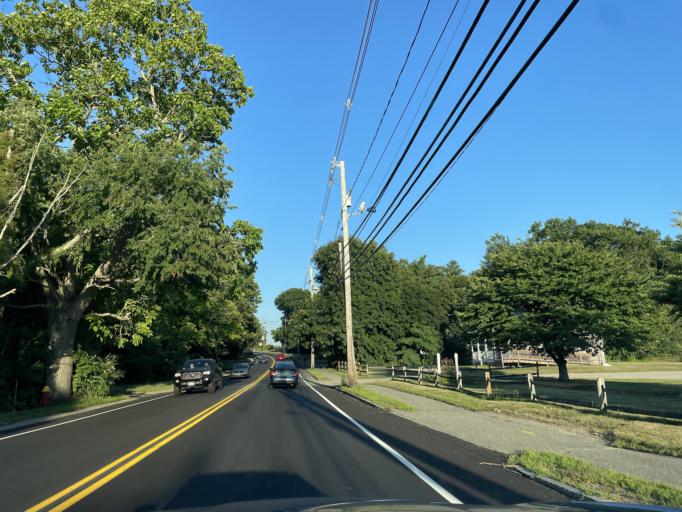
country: US
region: Massachusetts
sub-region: Plymouth County
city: Halifax
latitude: 41.9914
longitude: -70.8641
